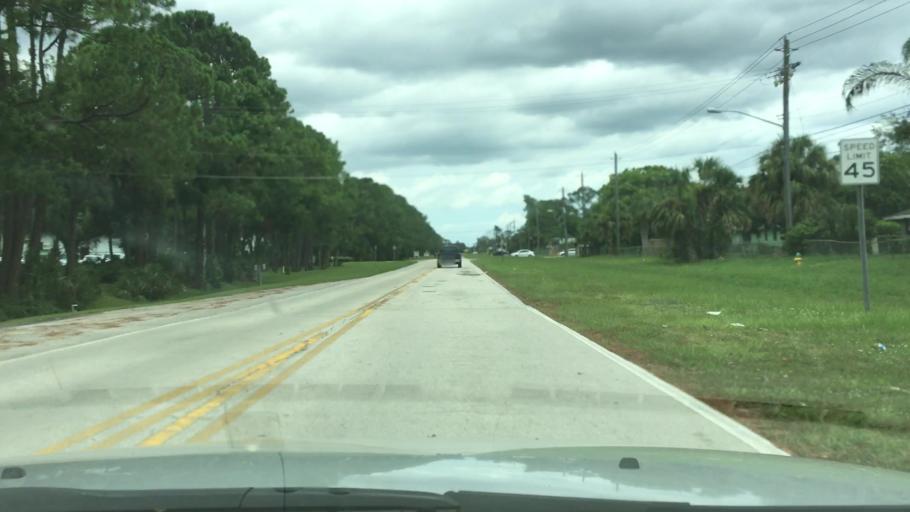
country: US
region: Florida
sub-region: Volusia County
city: Holly Hill
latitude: 29.2166
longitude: -81.0702
